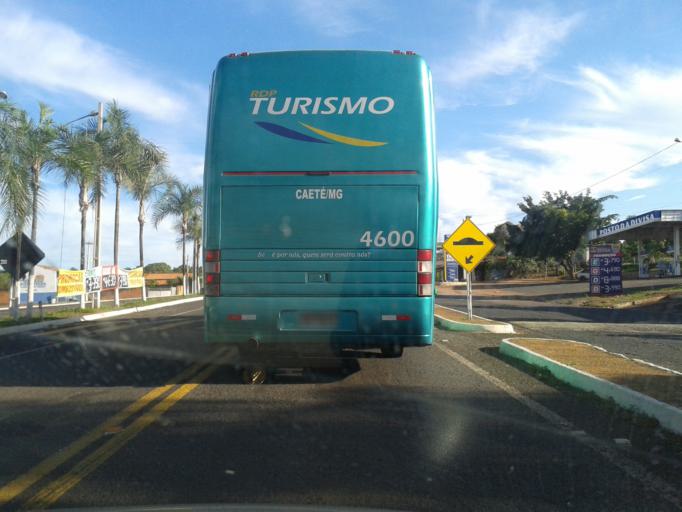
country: BR
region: Minas Gerais
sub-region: Tupaciguara
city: Tupaciguara
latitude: -18.3143
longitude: -48.5623
